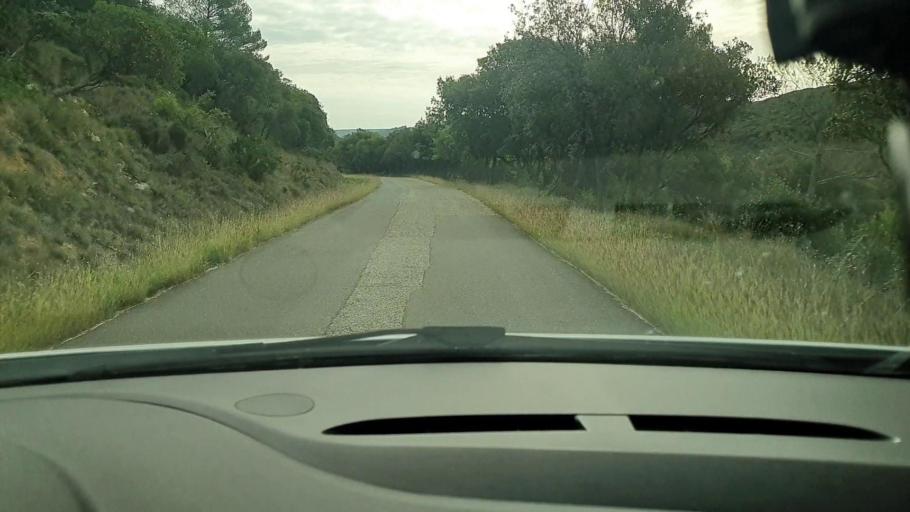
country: FR
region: Languedoc-Roussillon
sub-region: Departement du Gard
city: Montaren-et-Saint-Mediers
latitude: 44.0949
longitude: 4.3203
